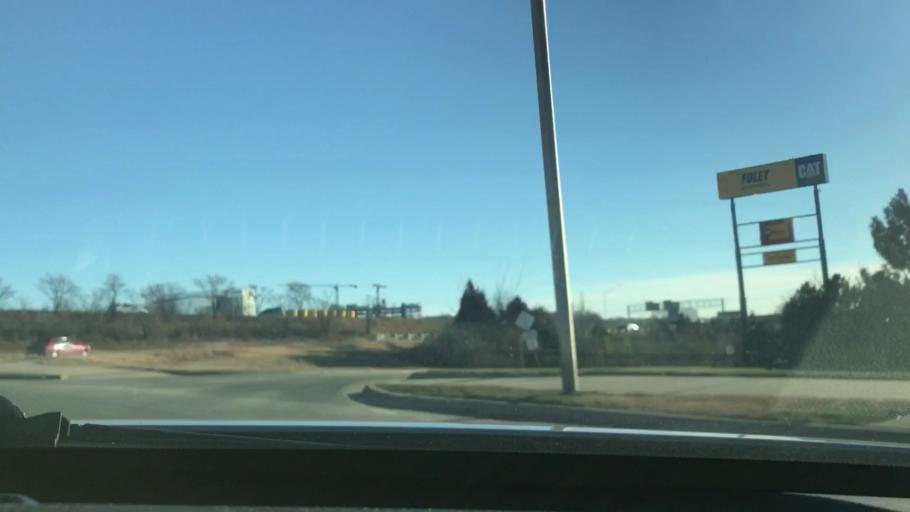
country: US
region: Missouri
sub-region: Jackson County
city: Raytown
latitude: 38.9673
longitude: -94.5213
